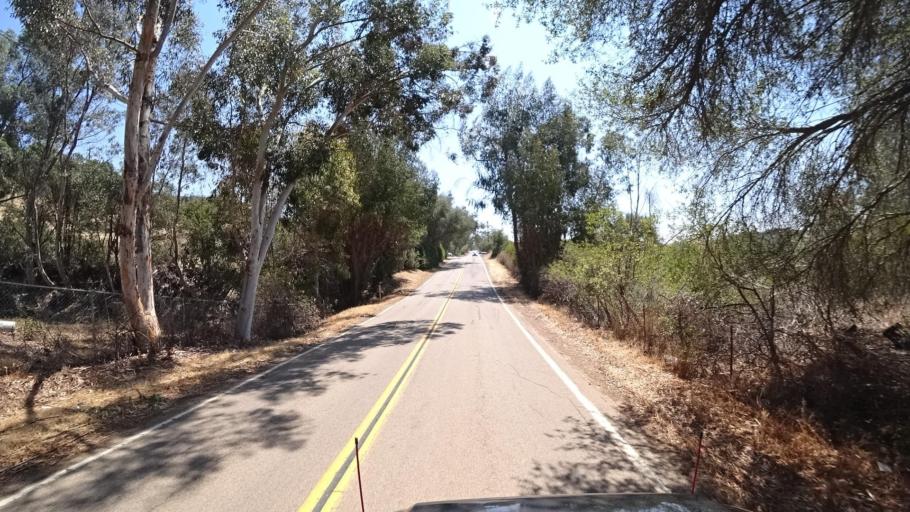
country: US
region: California
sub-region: San Diego County
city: Fallbrook
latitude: 33.4159
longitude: -117.3029
